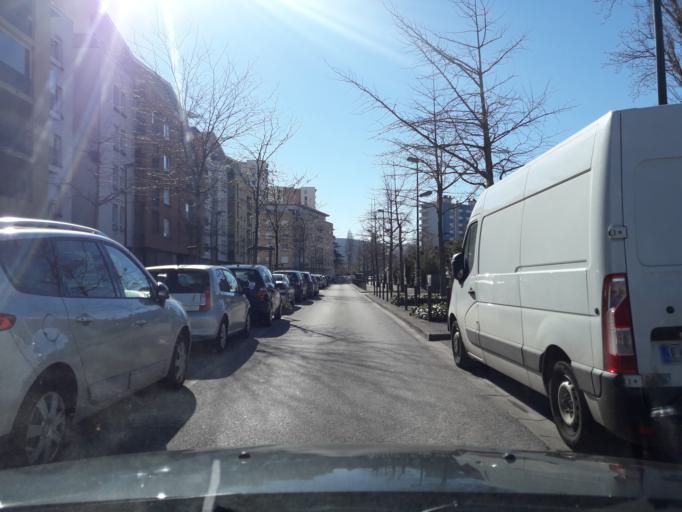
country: FR
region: Rhone-Alpes
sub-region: Departement de l'Isere
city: Echirolles
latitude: 45.1458
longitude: 5.7194
